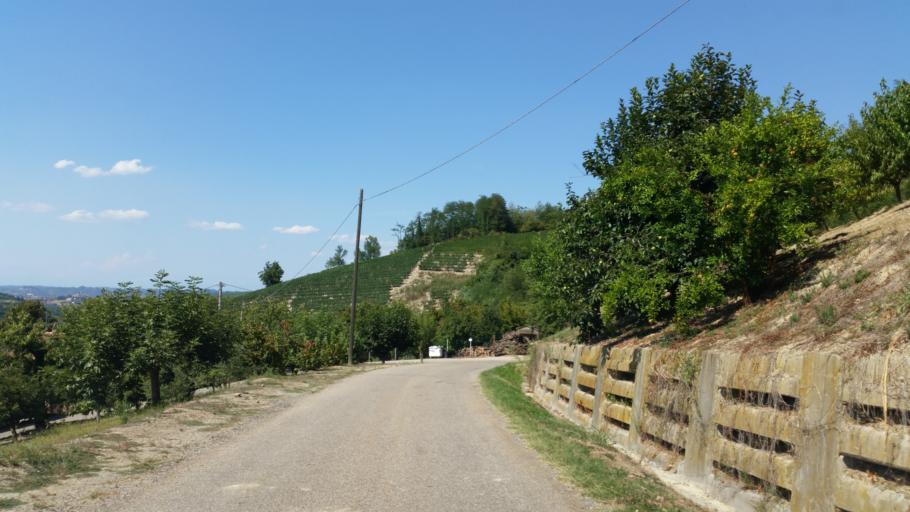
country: IT
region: Piedmont
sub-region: Provincia di Cuneo
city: Sinio
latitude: 44.6116
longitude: 8.0152
